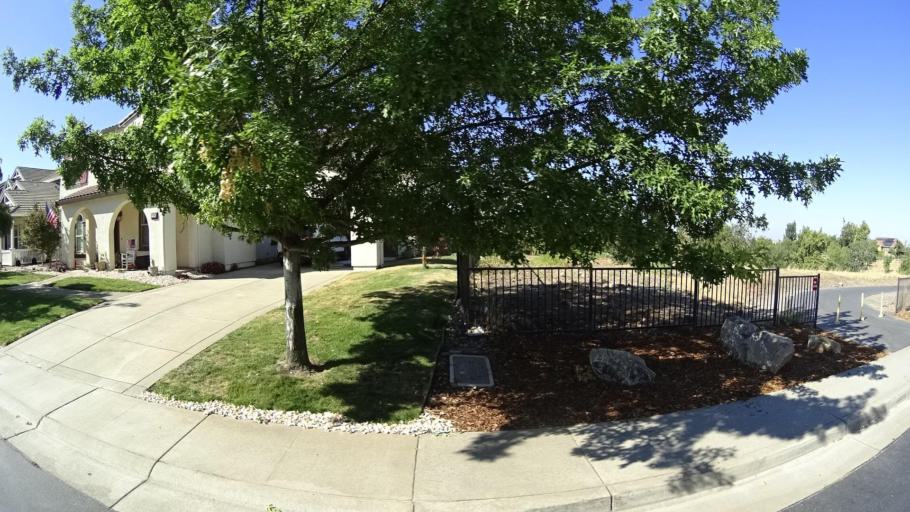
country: US
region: California
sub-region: Placer County
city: Lincoln
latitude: 38.8349
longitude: -121.2793
